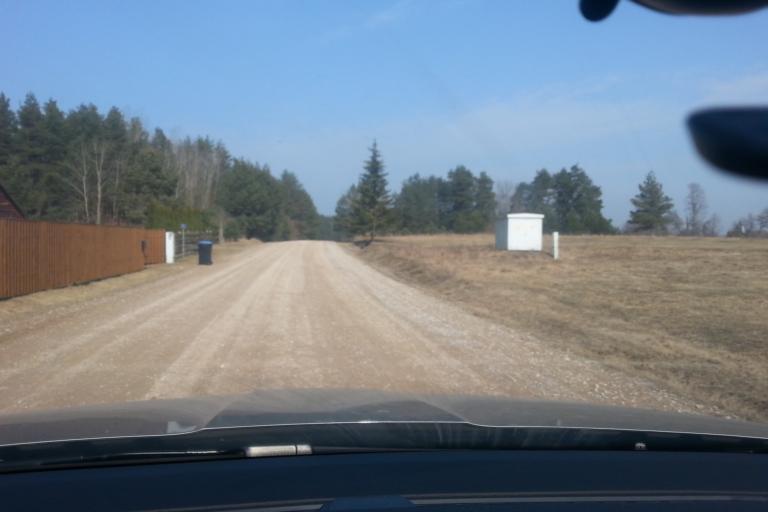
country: LT
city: Trakai
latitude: 54.5711
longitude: 24.9677
